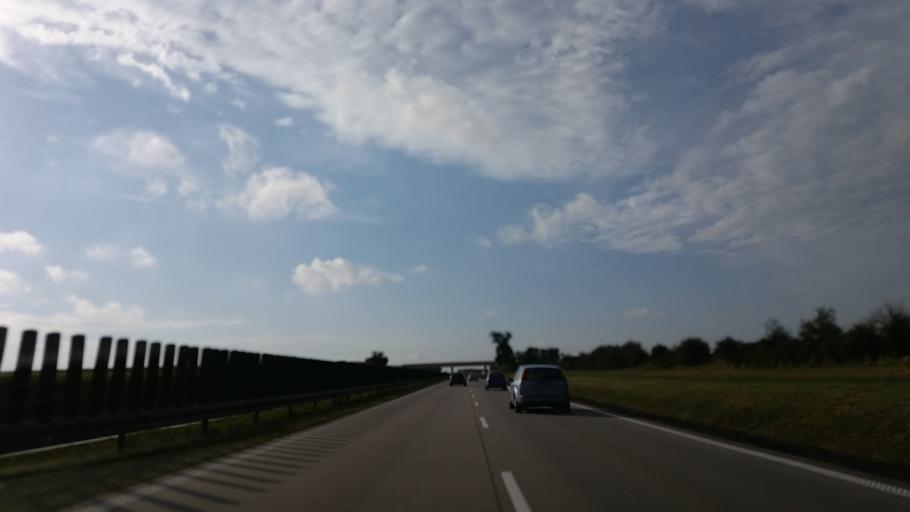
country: PL
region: Lower Silesian Voivodeship
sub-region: Powiat sredzki
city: Udanin
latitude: 51.1140
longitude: 16.3873
